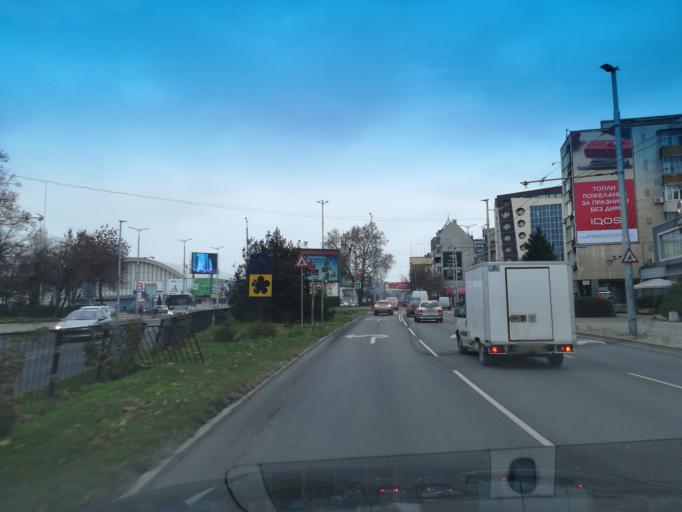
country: BG
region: Plovdiv
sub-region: Obshtina Plovdiv
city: Plovdiv
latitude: 42.1601
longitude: 24.7485
